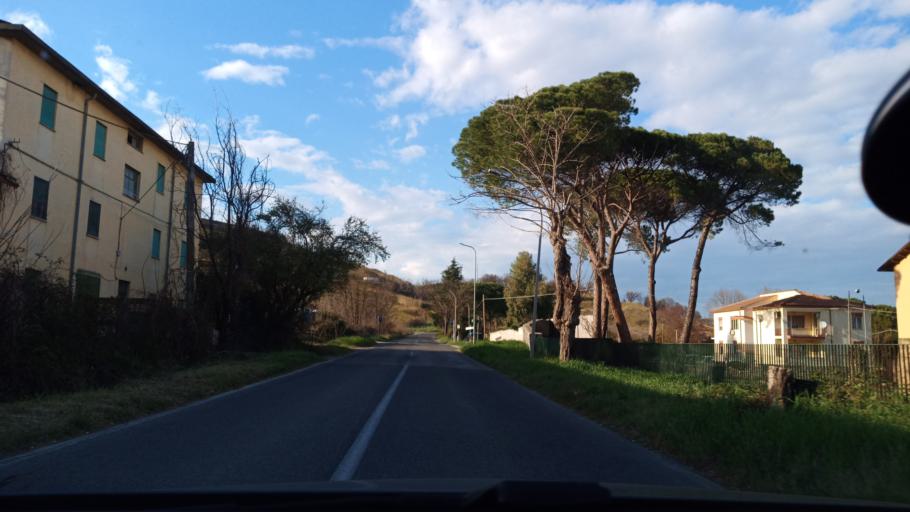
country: IT
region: Latium
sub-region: Citta metropolitana di Roma Capitale
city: Civitella San Paolo
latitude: 42.2009
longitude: 12.6054
